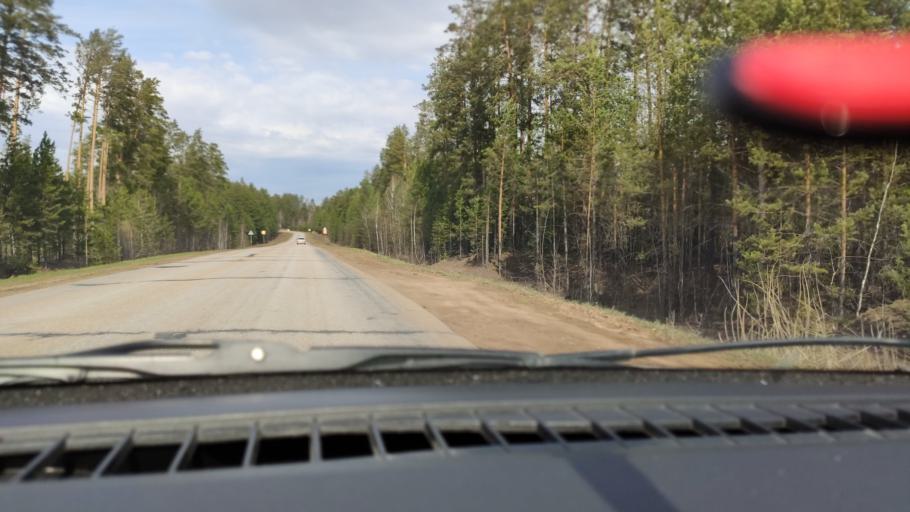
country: RU
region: Bashkortostan
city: Dyurtyuli
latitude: 55.5341
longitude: 54.8715
